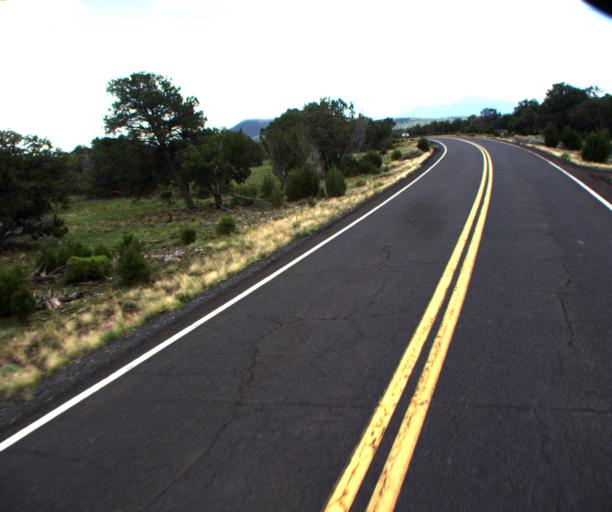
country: US
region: Arizona
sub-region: Coconino County
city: Parks
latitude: 35.5335
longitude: -111.8507
